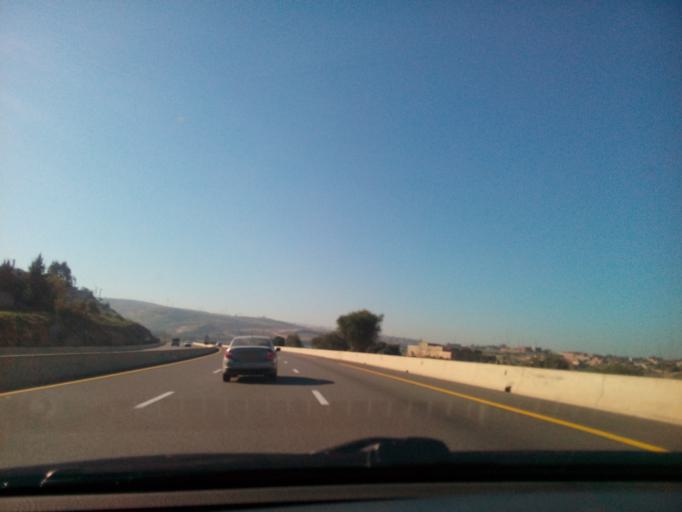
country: DZ
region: Chlef
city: Boukadir
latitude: 36.0638
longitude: 1.1508
